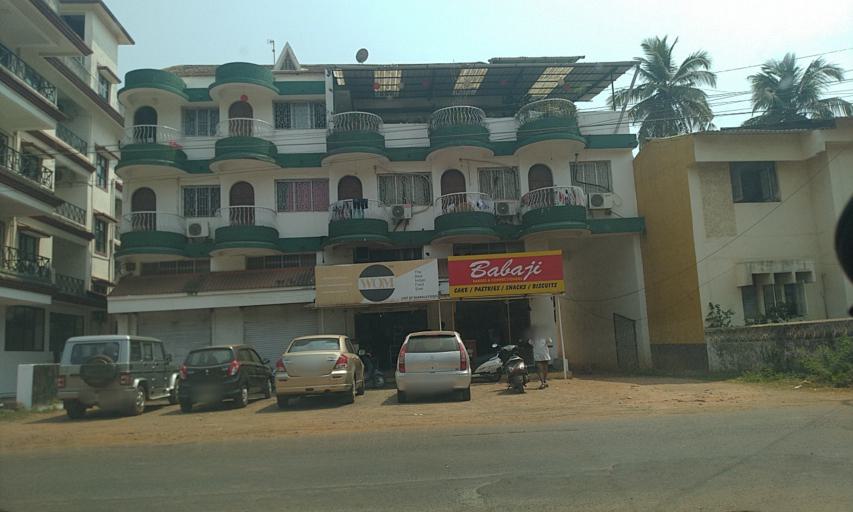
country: IN
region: Goa
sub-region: North Goa
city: Panaji
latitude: 15.4829
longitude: 73.8131
